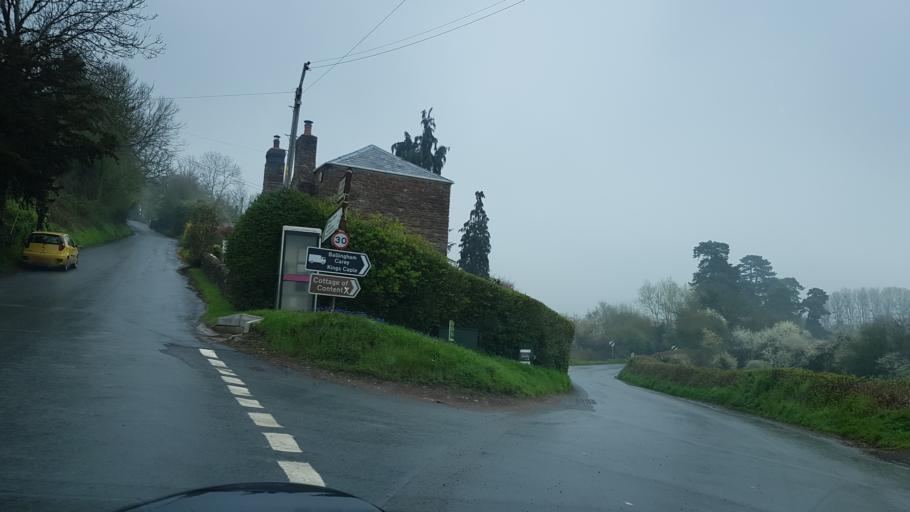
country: GB
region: England
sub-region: Herefordshire
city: Sellack
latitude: 51.9610
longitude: -2.6620
